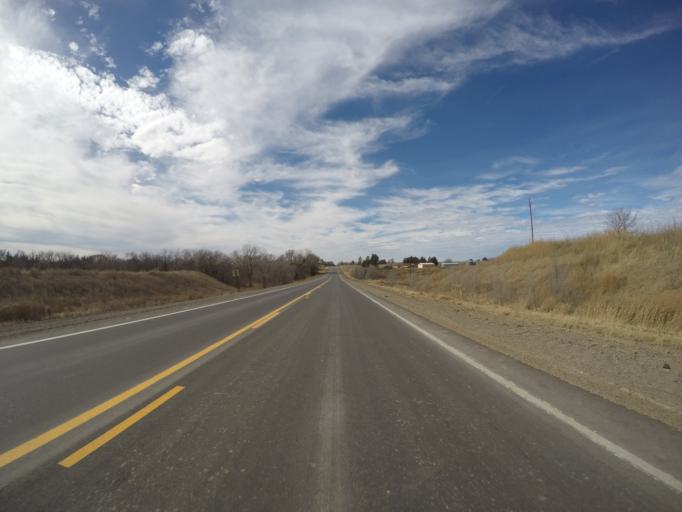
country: US
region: Nebraska
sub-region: Franklin County
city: Franklin
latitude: 40.0962
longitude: -98.9351
